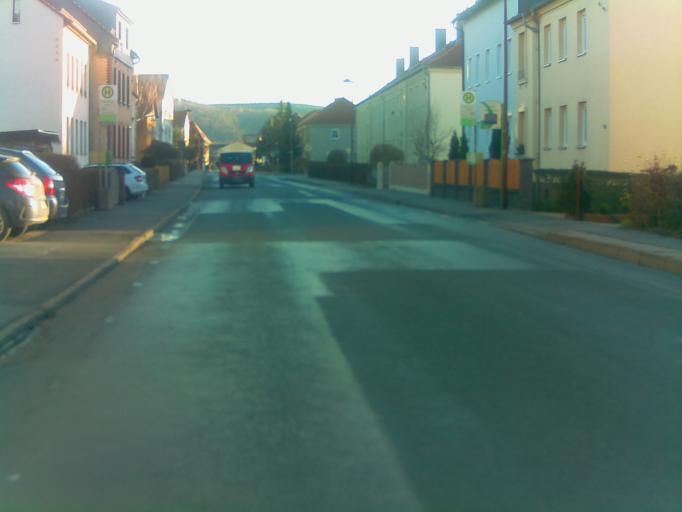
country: DE
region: Thuringia
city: Rudolstadt
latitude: 50.7030
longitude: 11.3258
